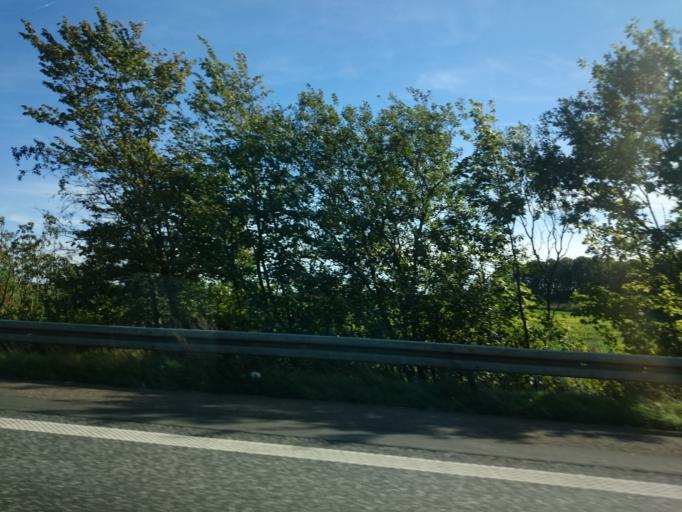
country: DK
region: Central Jutland
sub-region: Horsens Kommune
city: Horsens
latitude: 55.9481
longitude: 9.8262
